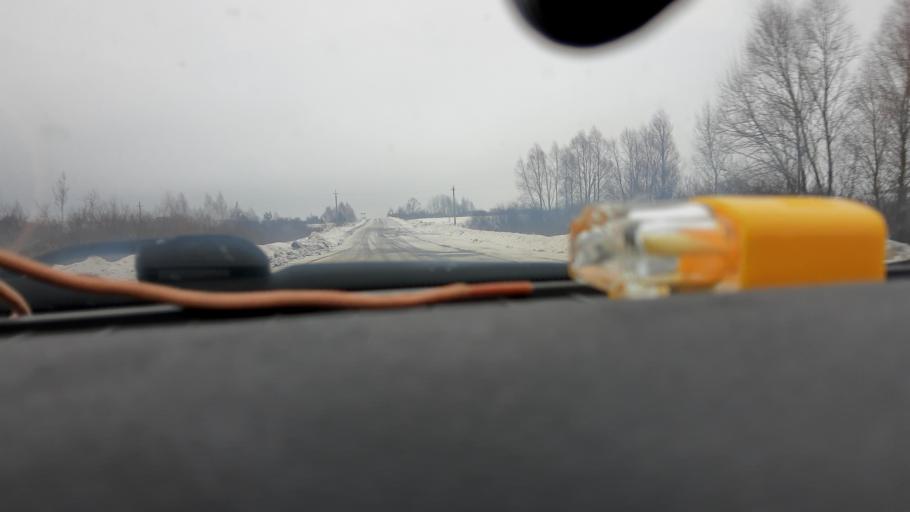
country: RU
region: Bashkortostan
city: Iglino
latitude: 54.6342
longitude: 56.4248
